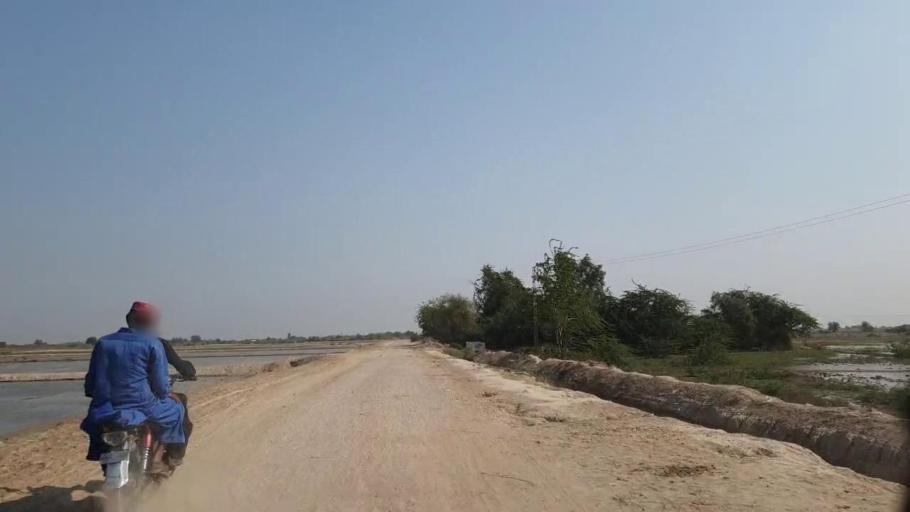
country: PK
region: Sindh
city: Bulri
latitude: 24.9347
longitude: 68.3653
